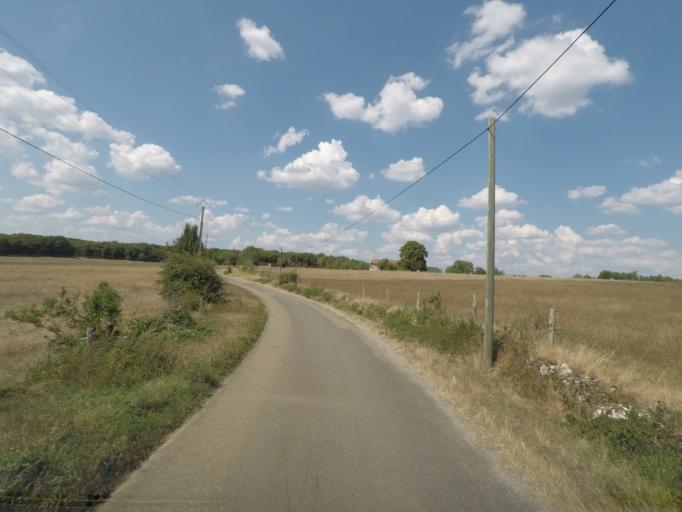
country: FR
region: Midi-Pyrenees
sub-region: Departement du Lot
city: Cahors
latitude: 44.5316
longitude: 1.6146
